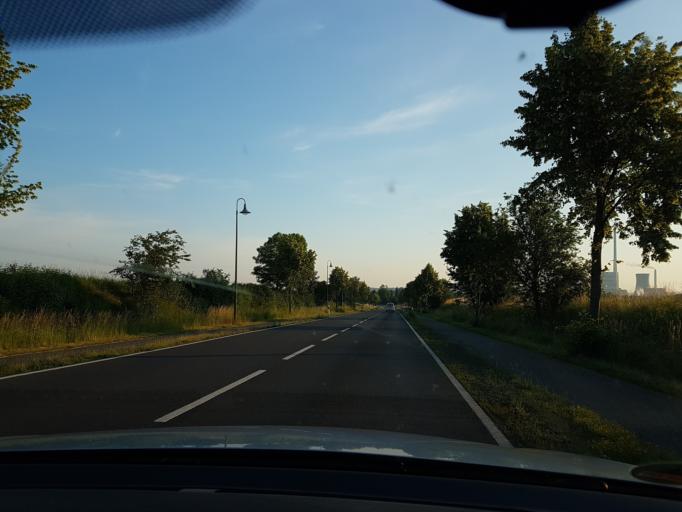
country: DE
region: Lower Saxony
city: Schoningen
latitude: 52.1506
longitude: 10.9662
